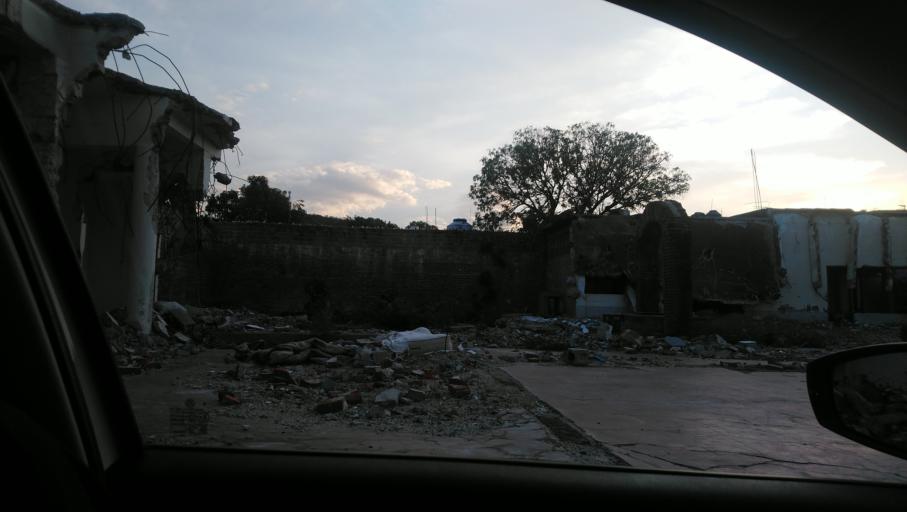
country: MX
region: Oaxaca
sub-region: Salina Cruz
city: Salina Cruz
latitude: 16.1834
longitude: -95.1975
